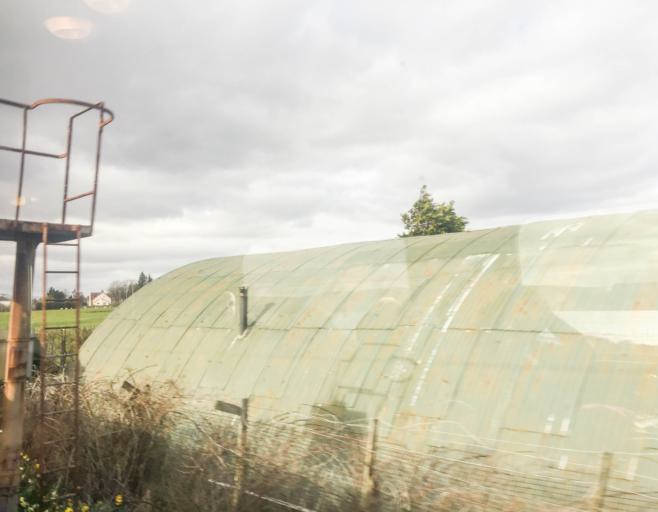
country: GB
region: Scotland
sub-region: Argyll and Bute
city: Cardross
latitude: 55.9544
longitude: -4.6410
